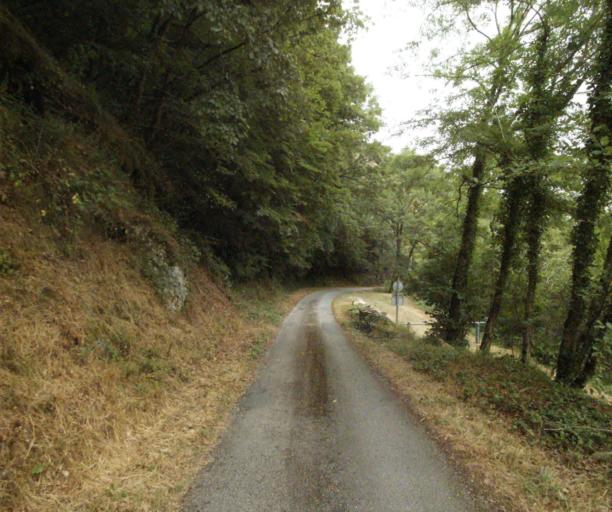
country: FR
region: Midi-Pyrenees
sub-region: Departement du Tarn
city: Soreze
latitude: 43.4202
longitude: 2.0841
